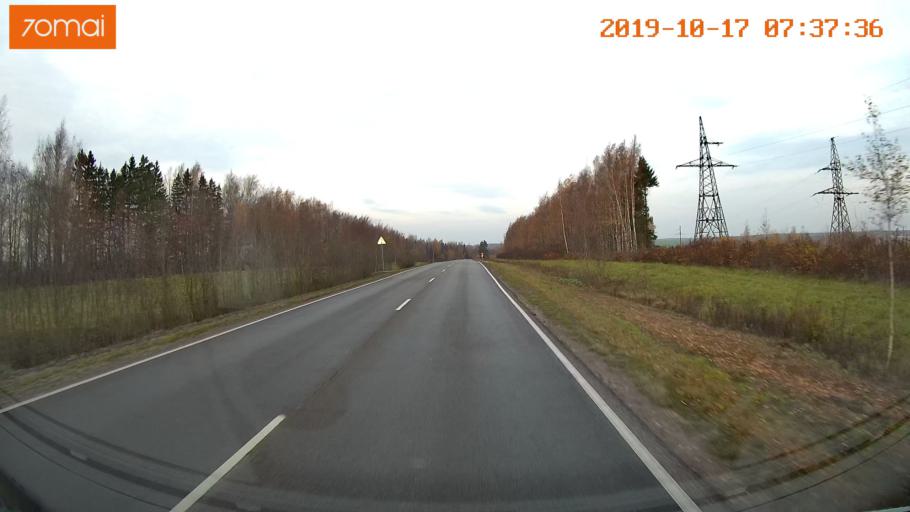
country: RU
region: Vladimir
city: Yur'yev-Pol'skiy
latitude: 56.4502
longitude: 39.8951
